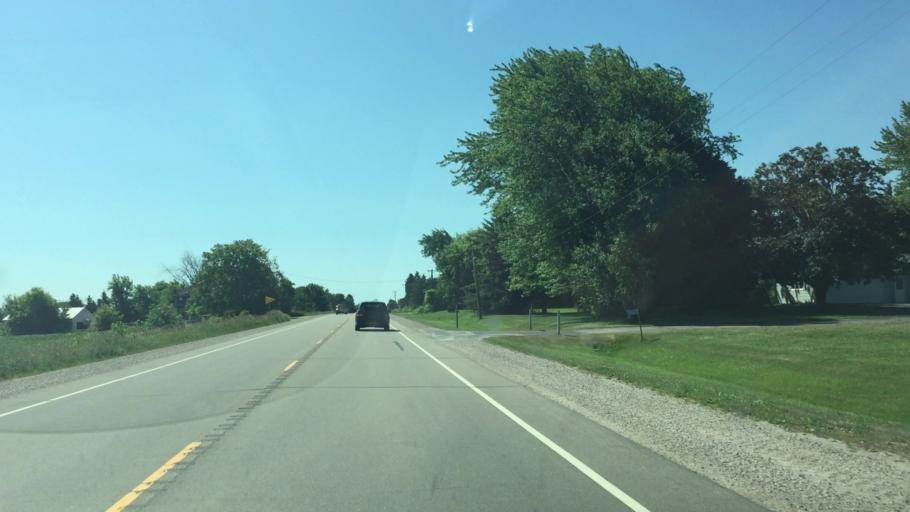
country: US
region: Wisconsin
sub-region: Calumet County
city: New Holstein
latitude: 43.9840
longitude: -88.1169
